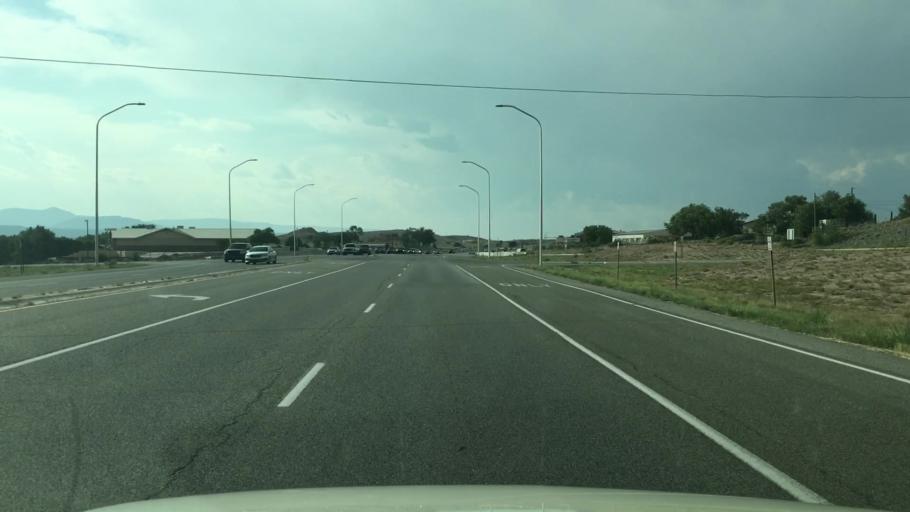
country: US
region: New Mexico
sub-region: Santa Fe County
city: El Valle de Arroyo Seco
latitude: 35.9686
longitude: -106.0370
